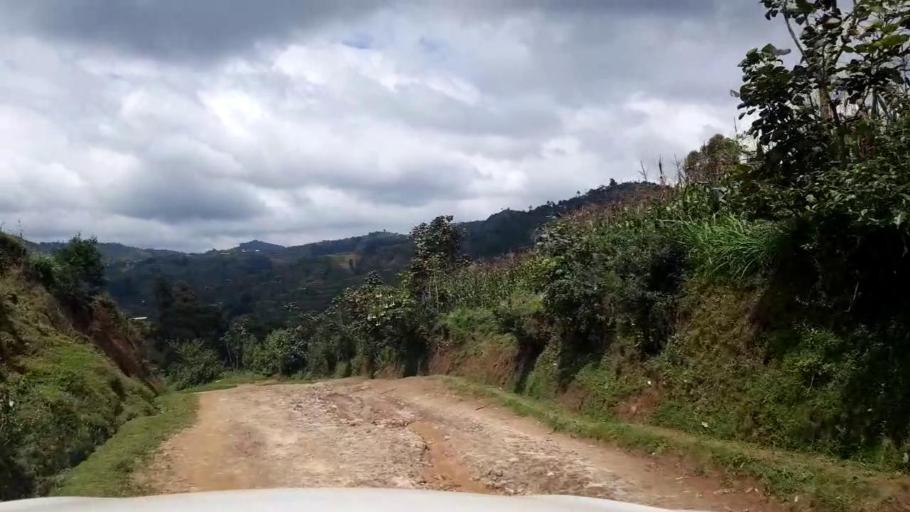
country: RW
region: Western Province
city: Kibuye
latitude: -1.9209
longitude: 29.4563
